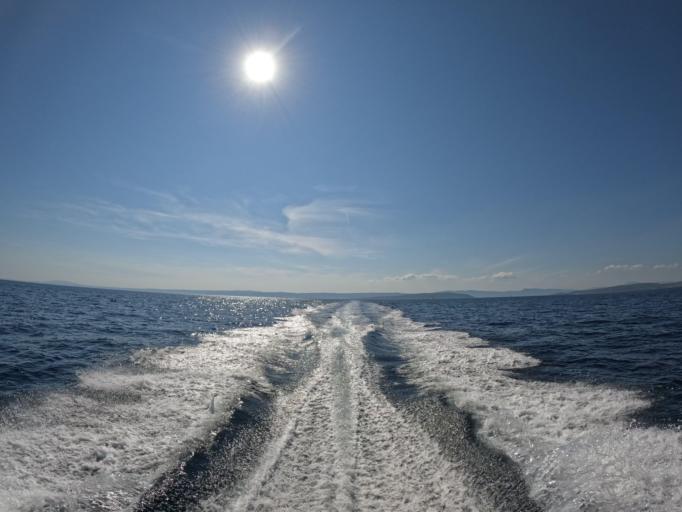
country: HR
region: Primorsko-Goranska
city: Punat
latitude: 44.9586
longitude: 14.6371
